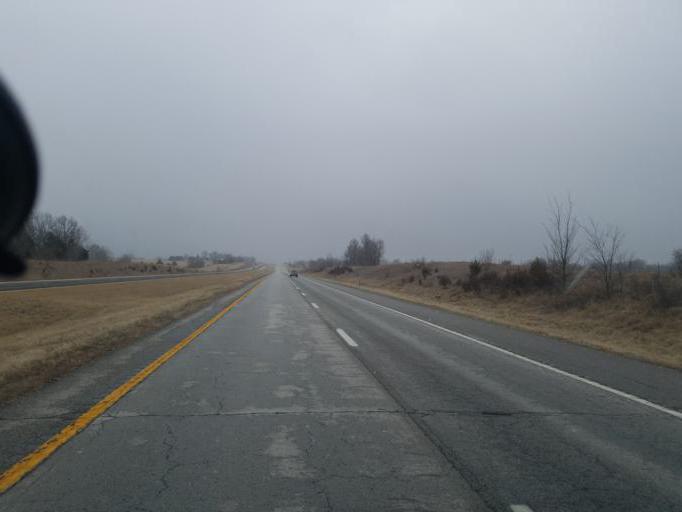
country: US
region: Missouri
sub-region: Macon County
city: La Plata
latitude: 39.9097
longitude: -92.4735
